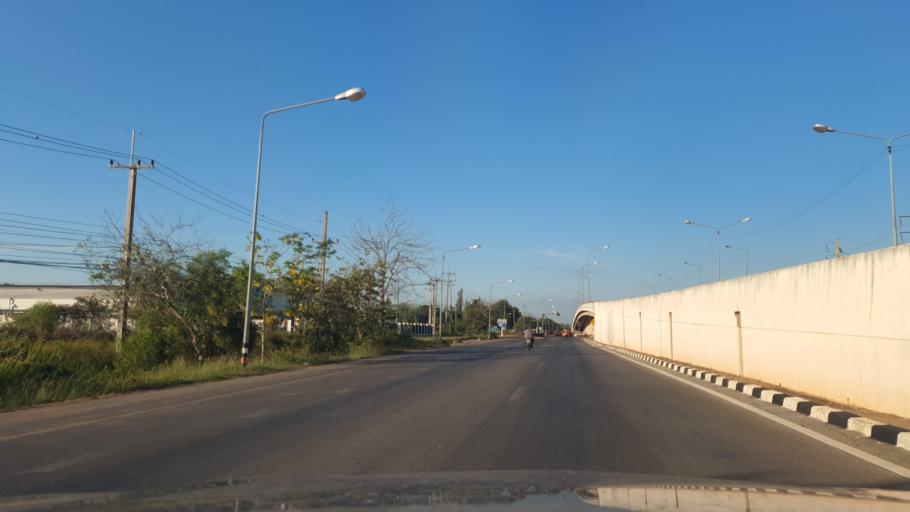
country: TH
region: Phitsanulok
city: Phitsanulok
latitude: 16.8636
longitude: 100.2164
